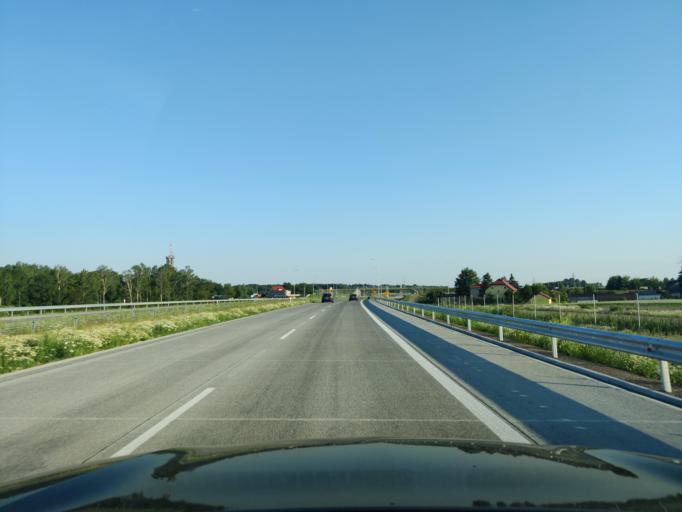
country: PL
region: Masovian Voivodeship
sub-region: Powiat mlawski
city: Mlawa
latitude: 53.1034
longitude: 20.4126
